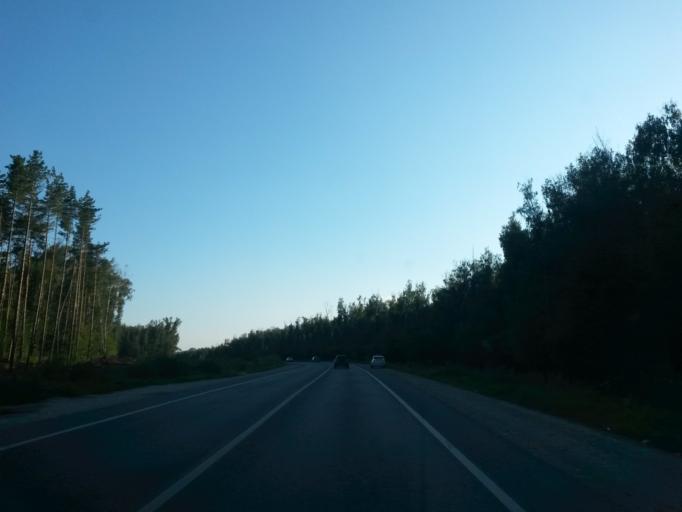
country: RU
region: Moskovskaya
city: Vostryakovo
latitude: 55.4281
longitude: 37.8539
